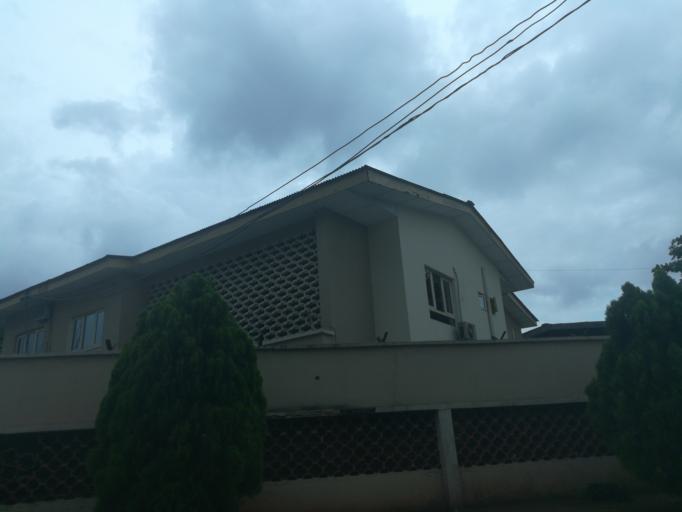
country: NG
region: Lagos
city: Ikeja
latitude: 6.6164
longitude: 3.3465
